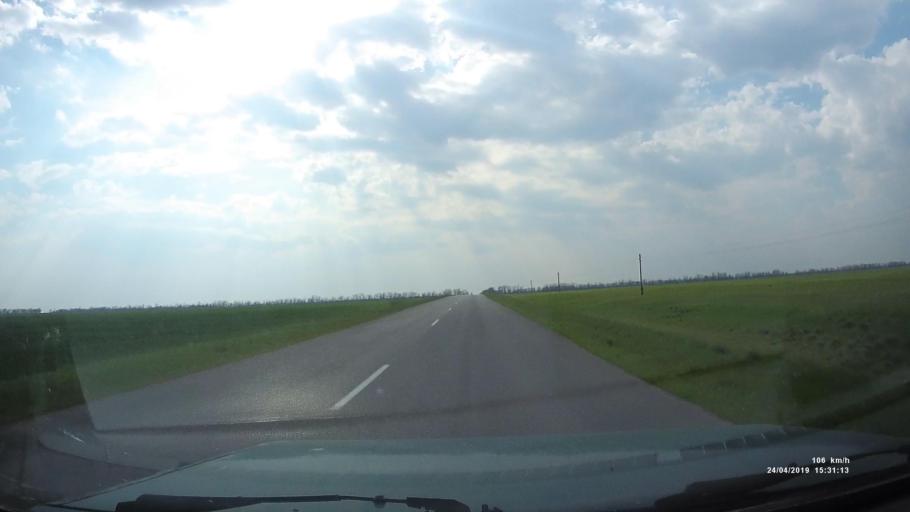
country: RU
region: Rostov
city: Remontnoye
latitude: 46.5997
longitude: 42.9885
